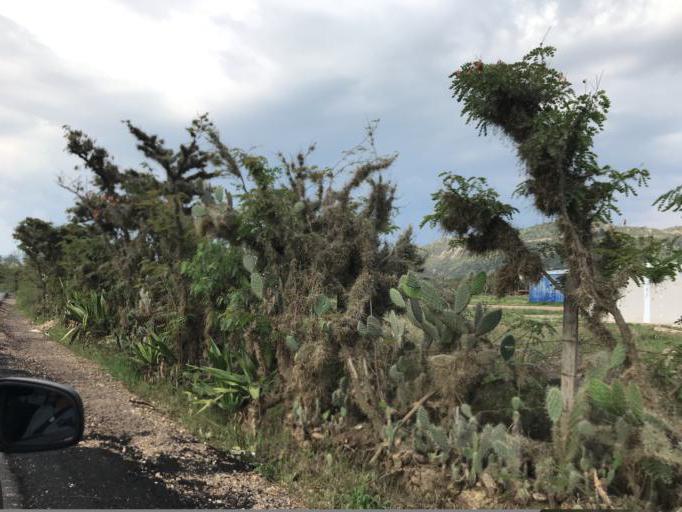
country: CO
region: Boyaca
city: Villa de Leiva
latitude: 5.6405
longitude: -73.5979
